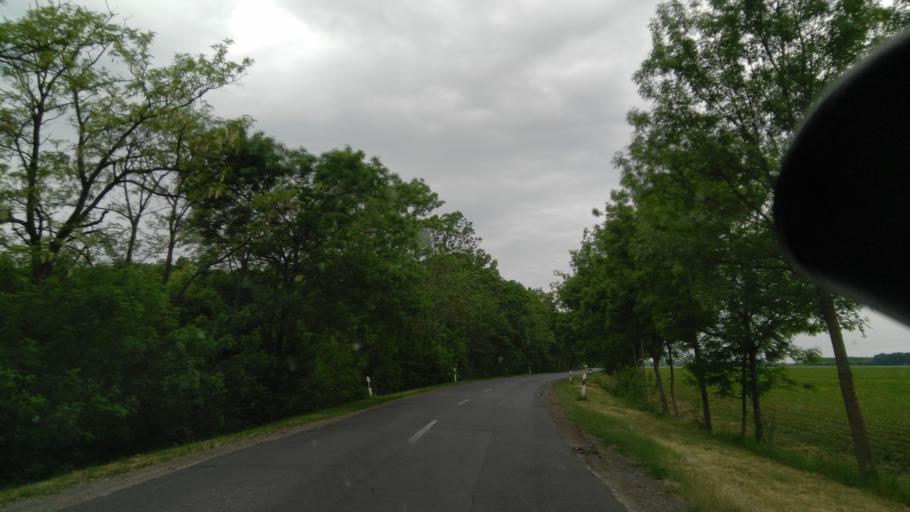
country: HU
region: Bekes
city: Doboz
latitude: 46.7239
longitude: 21.2978
